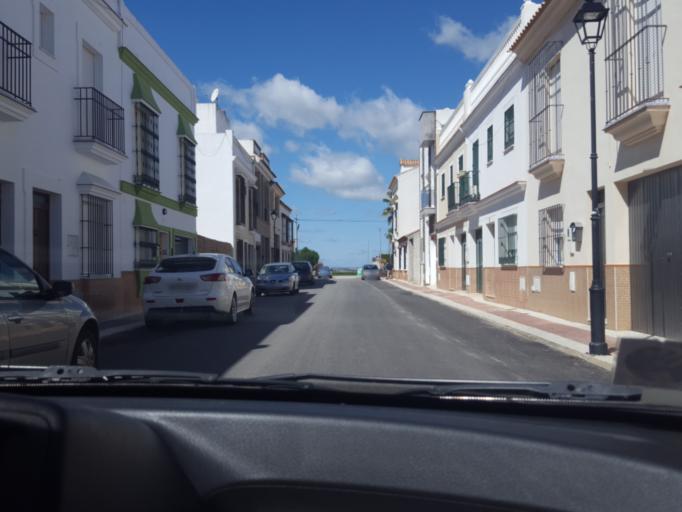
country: ES
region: Andalusia
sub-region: Provincia de Sevilla
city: Acala del Rio
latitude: 37.5194
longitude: -5.9853
